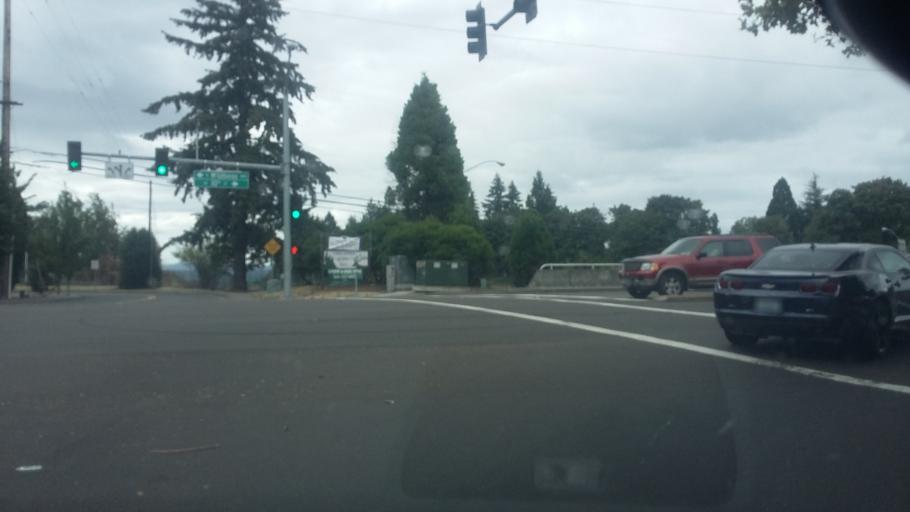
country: US
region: Washington
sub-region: Clark County
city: Orchards
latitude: 45.6149
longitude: -122.5536
